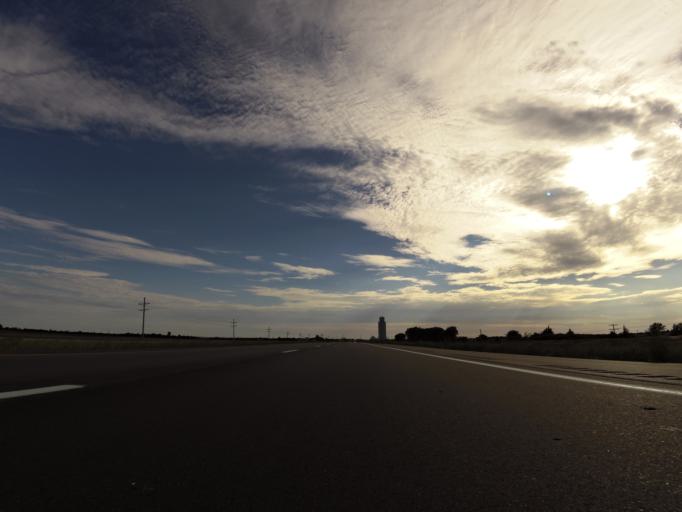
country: US
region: Kansas
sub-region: Reno County
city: South Hutchinson
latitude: 38.0111
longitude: -98.0081
